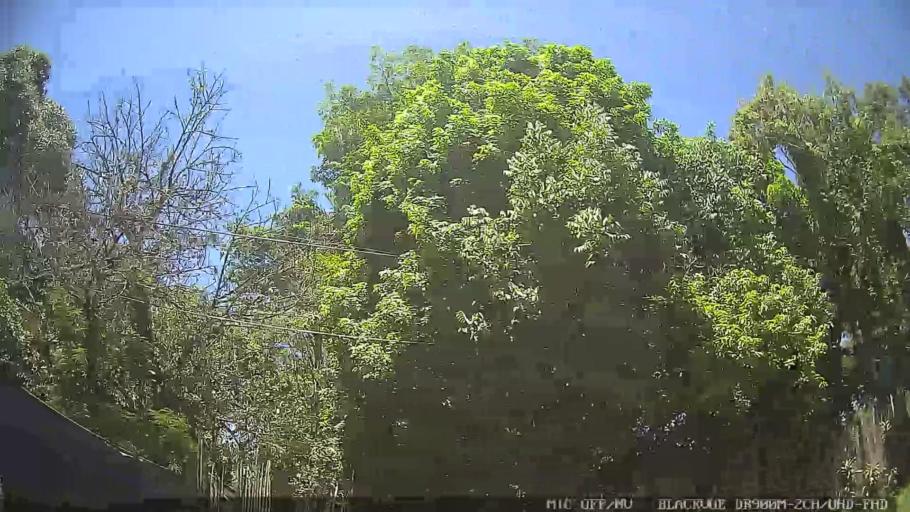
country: BR
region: Sao Paulo
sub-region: Pedreira
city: Pedreira
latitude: -22.7433
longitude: -46.9274
